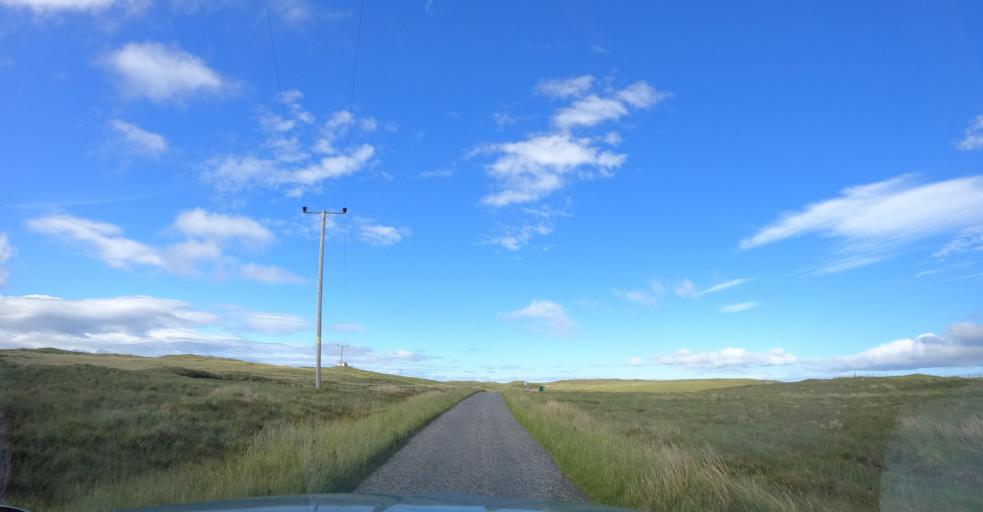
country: GB
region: Scotland
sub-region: Eilean Siar
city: Stornoway
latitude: 58.1760
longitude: -6.5547
